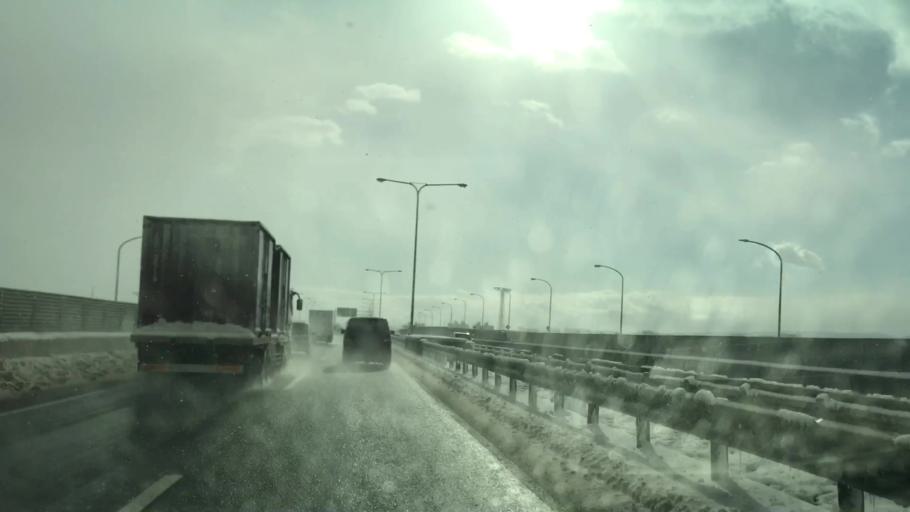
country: JP
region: Hokkaido
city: Sapporo
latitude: 43.0491
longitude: 141.4325
